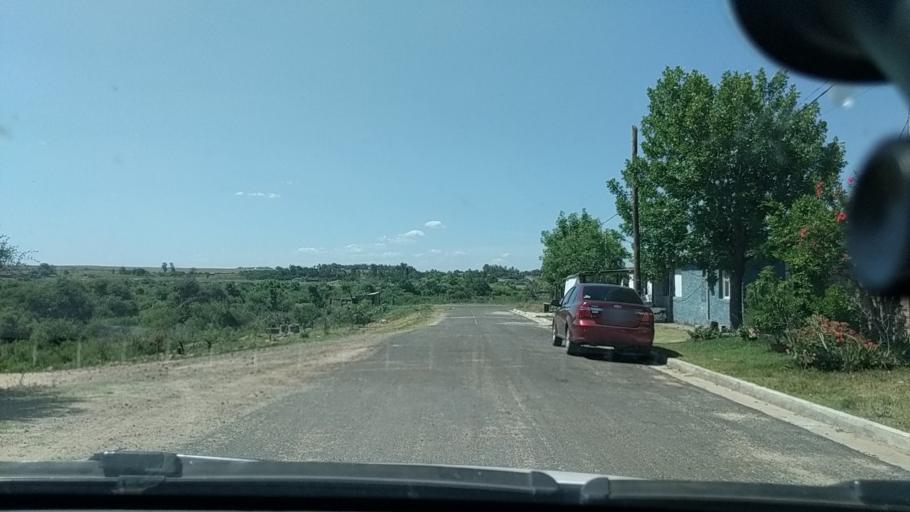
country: UY
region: Tacuarembo
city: Paso de los Toros
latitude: -32.8087
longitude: -56.5317
